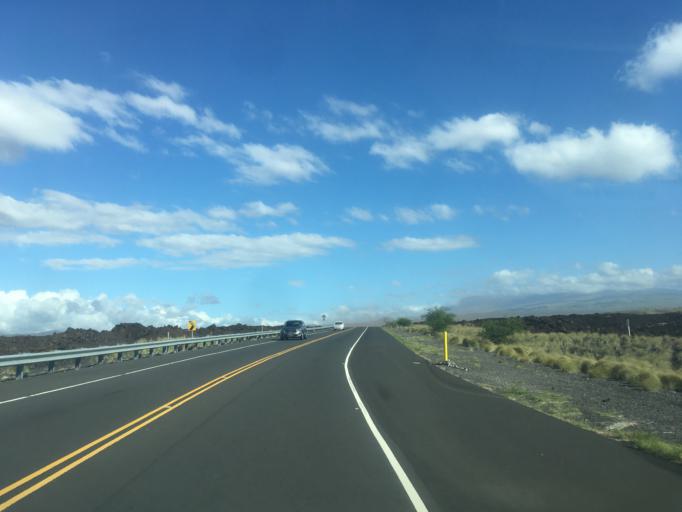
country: US
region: Hawaii
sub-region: Hawaii County
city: Waikoloa Village
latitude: 19.9159
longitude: -155.8303
